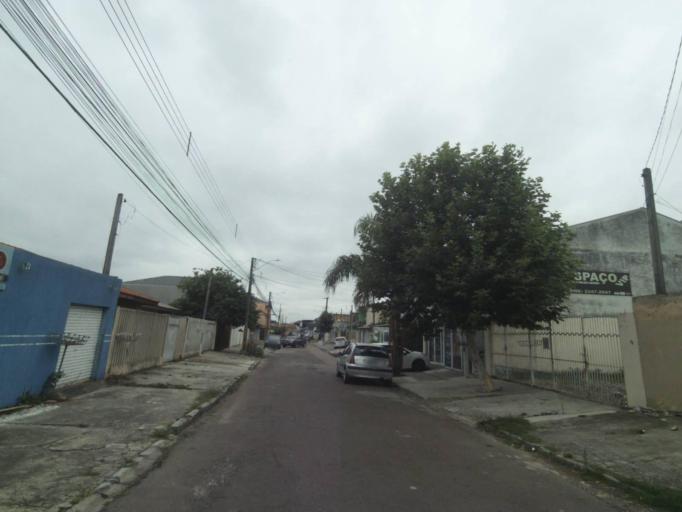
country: BR
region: Parana
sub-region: Araucaria
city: Araucaria
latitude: -25.5452
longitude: -49.3405
